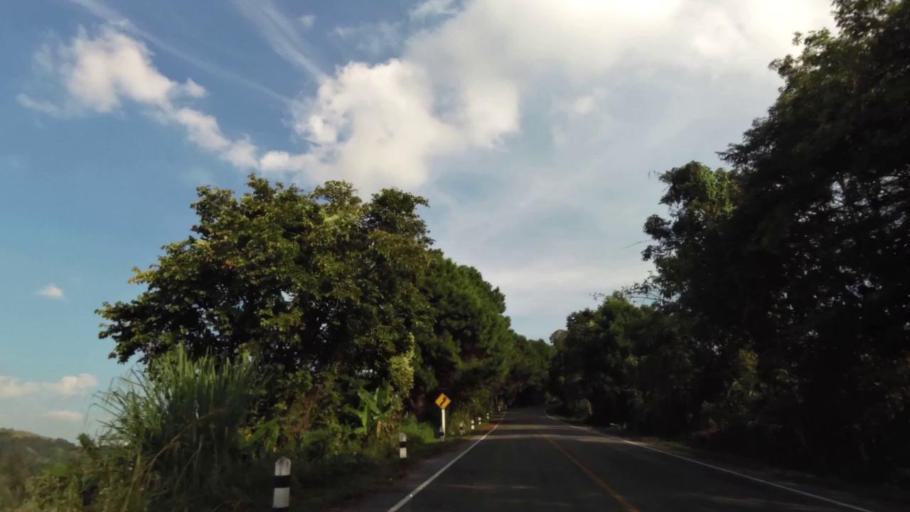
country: TH
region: Chiang Rai
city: Khun Tan
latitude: 19.8709
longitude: 100.3249
